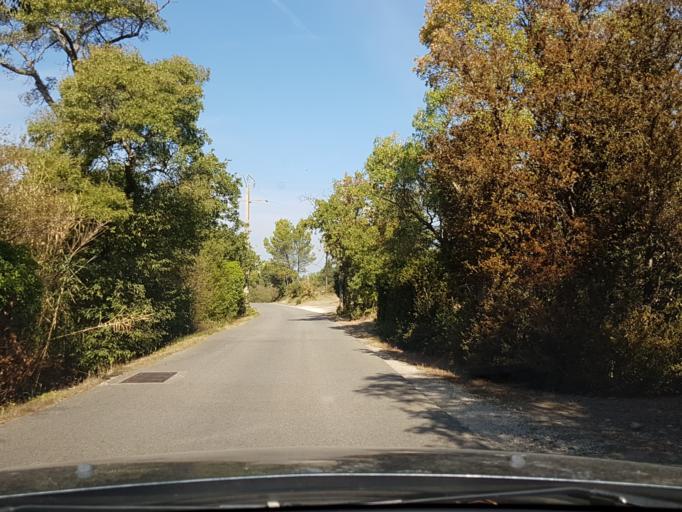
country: FR
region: Provence-Alpes-Cote d'Azur
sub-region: Departement des Bouches-du-Rhone
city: Eygalieres
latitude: 43.7681
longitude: 4.9614
